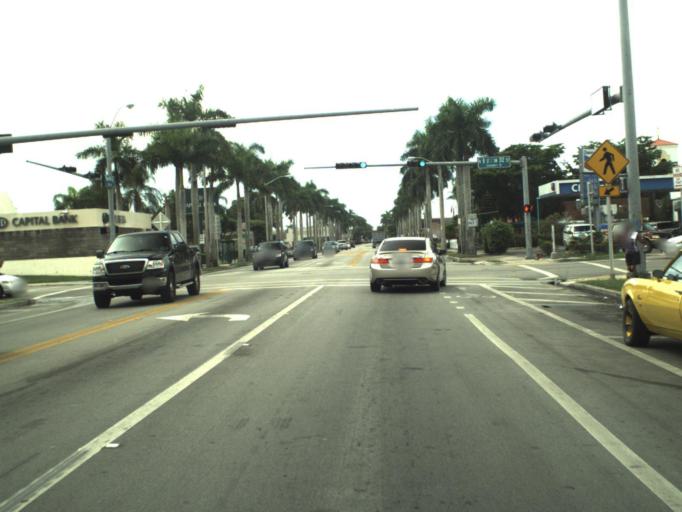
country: US
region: Florida
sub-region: Miami-Dade County
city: Homestead
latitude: 25.4775
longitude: -80.4775
